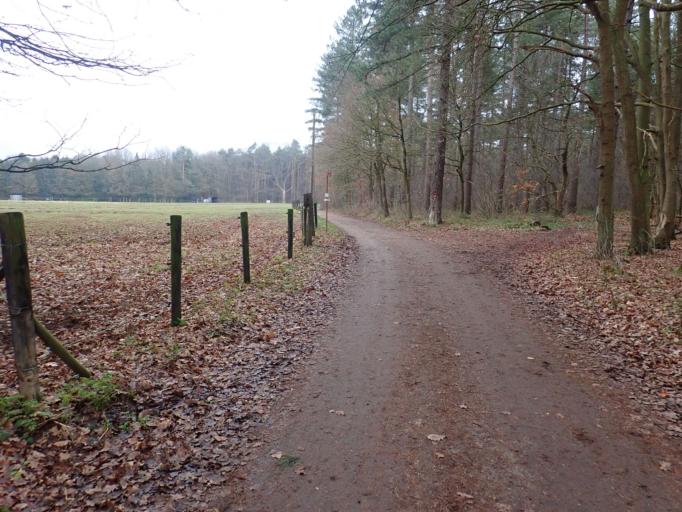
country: BE
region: Flanders
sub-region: Provincie Antwerpen
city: Zandhoven
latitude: 51.2288
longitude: 4.6376
